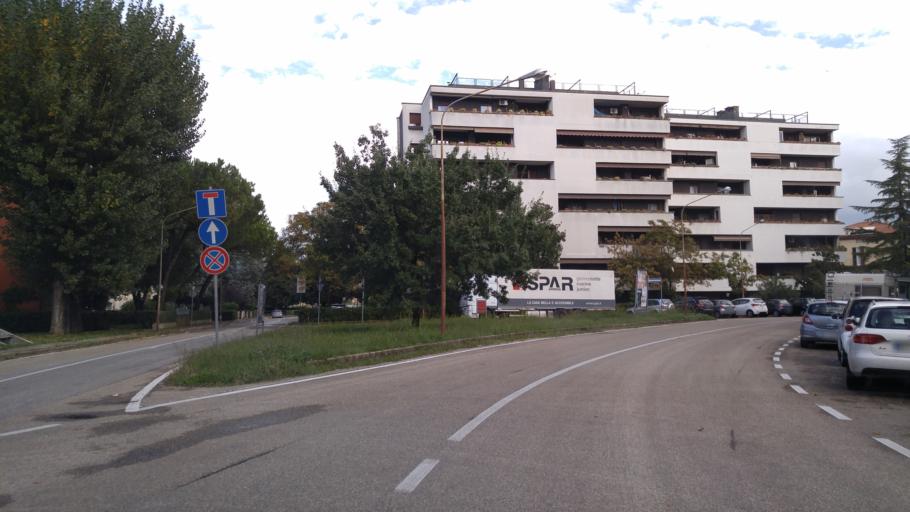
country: IT
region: The Marches
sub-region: Provincia di Pesaro e Urbino
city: Pesaro
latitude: 43.8962
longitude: 12.8995
